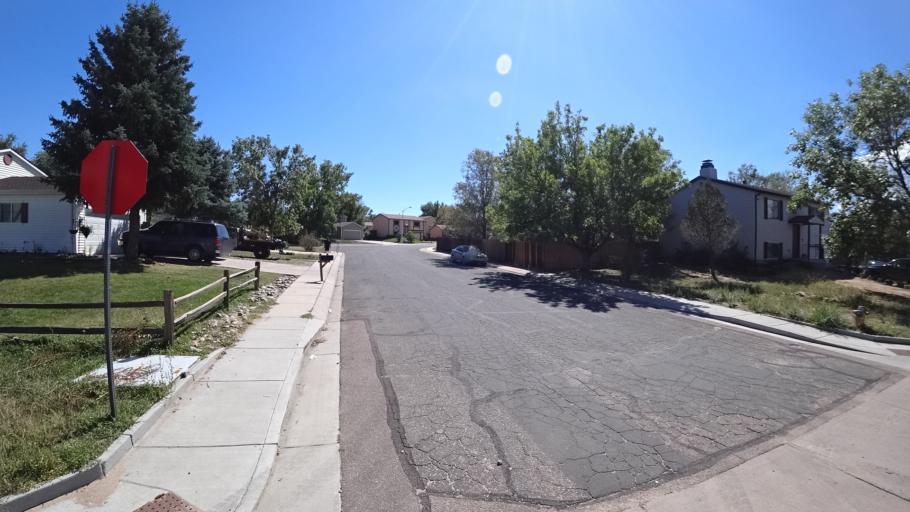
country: US
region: Colorado
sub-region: El Paso County
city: Stratmoor
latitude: 38.7864
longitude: -104.7438
